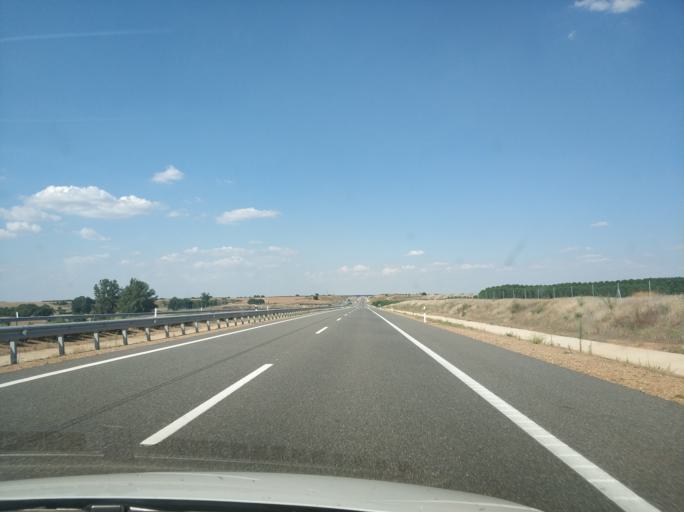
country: ES
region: Castille and Leon
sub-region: Provincia de Zamora
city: Santovenia
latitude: 41.8788
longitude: -5.6980
